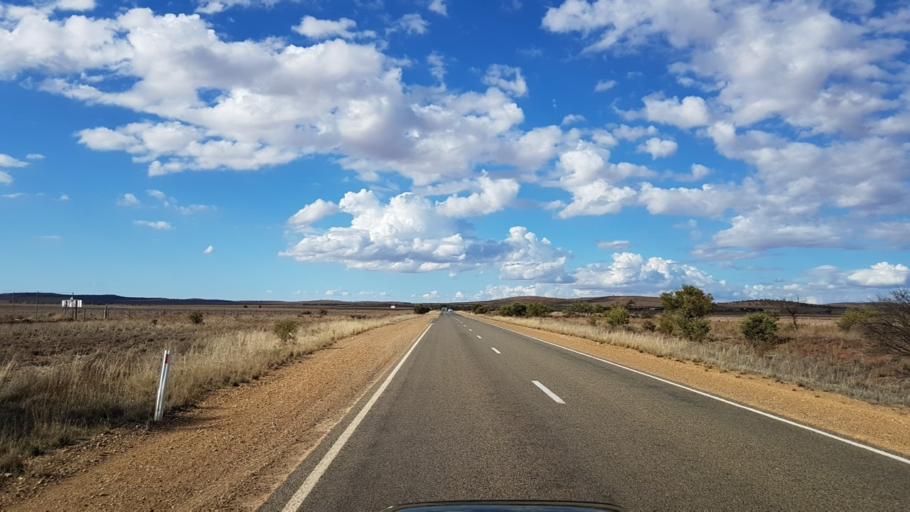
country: AU
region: South Australia
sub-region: Peterborough
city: Peterborough
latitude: -32.9679
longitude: 138.8706
